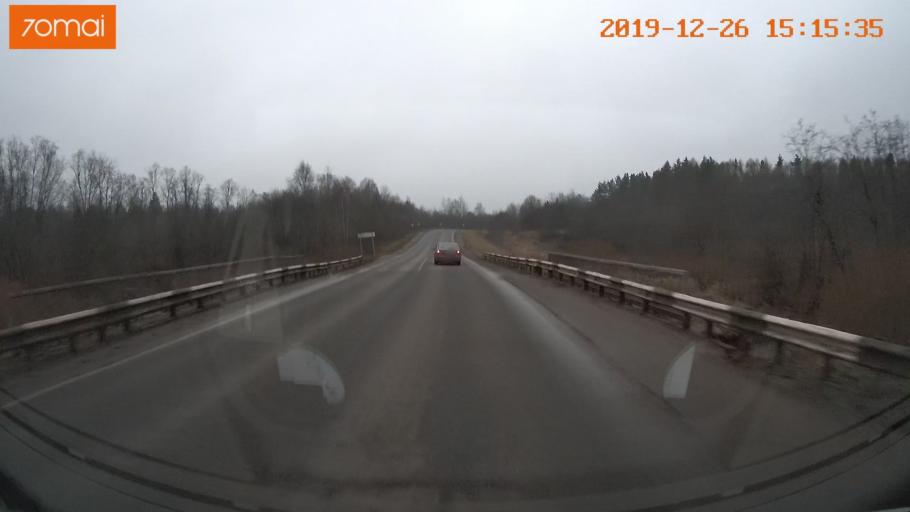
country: RU
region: Jaroslavl
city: Rybinsk
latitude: 58.0953
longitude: 38.8743
